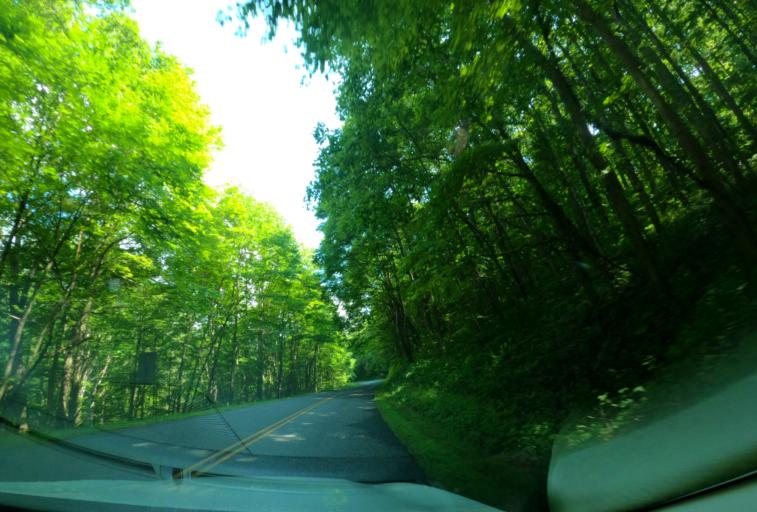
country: US
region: North Carolina
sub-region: Haywood County
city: Hazelwood
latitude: 35.4366
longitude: -83.0800
